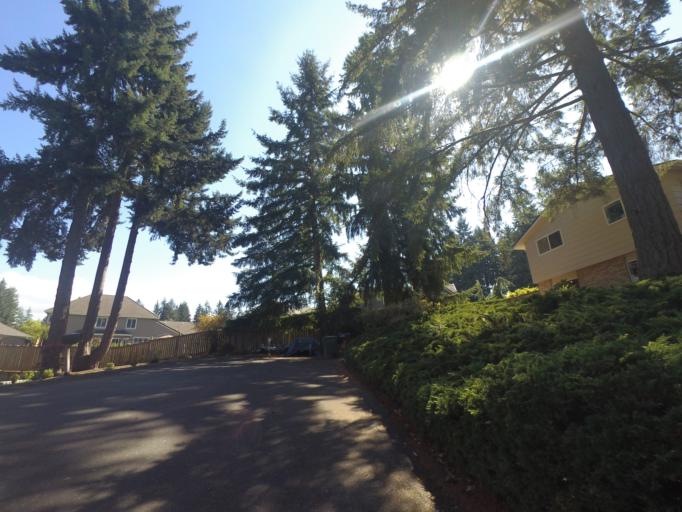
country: US
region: Washington
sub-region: Pierce County
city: Fircrest
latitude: 47.2140
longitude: -122.5184
